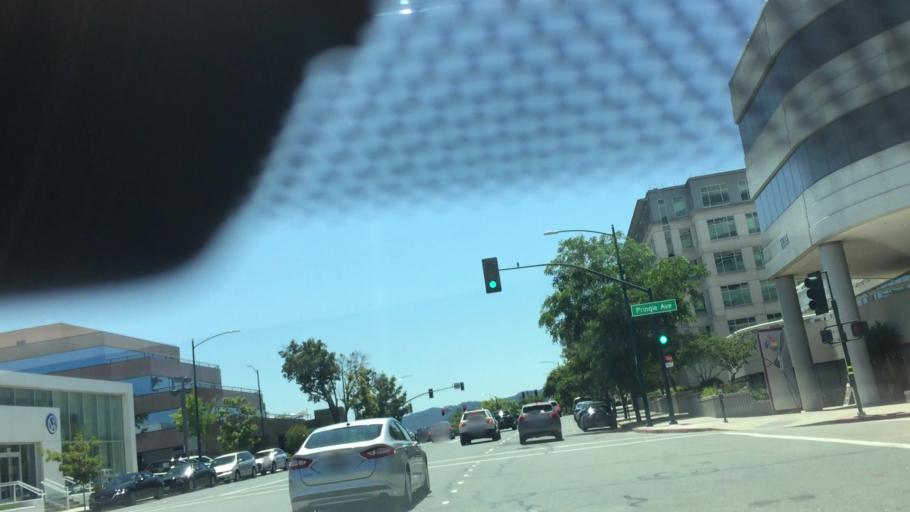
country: US
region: California
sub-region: Contra Costa County
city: Walnut Creek
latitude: 37.9077
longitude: -122.0649
